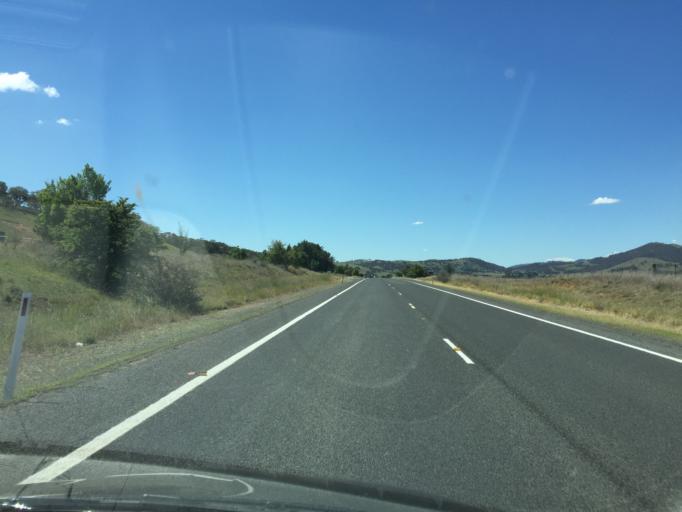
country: AU
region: Australian Capital Territory
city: Macarthur
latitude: -35.7281
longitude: 149.1601
